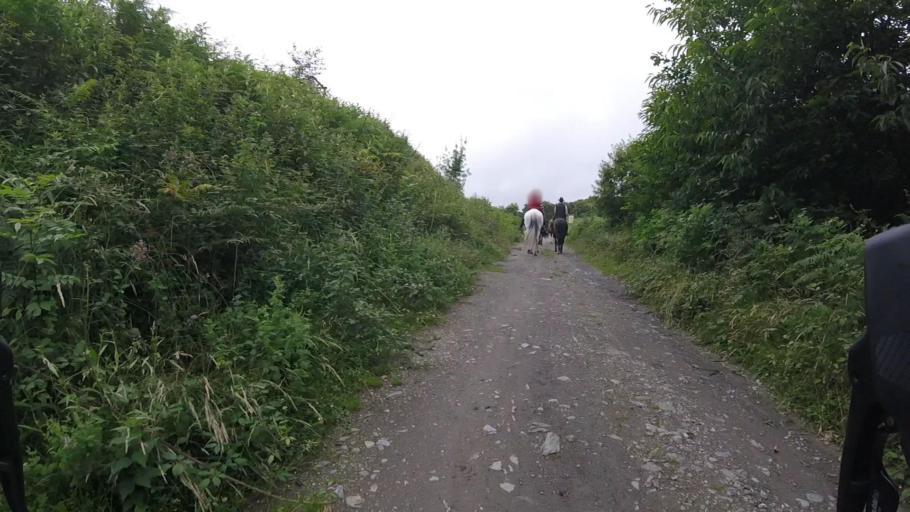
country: ES
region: Navarre
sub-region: Provincia de Navarra
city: Arano
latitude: 43.2513
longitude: -1.8909
